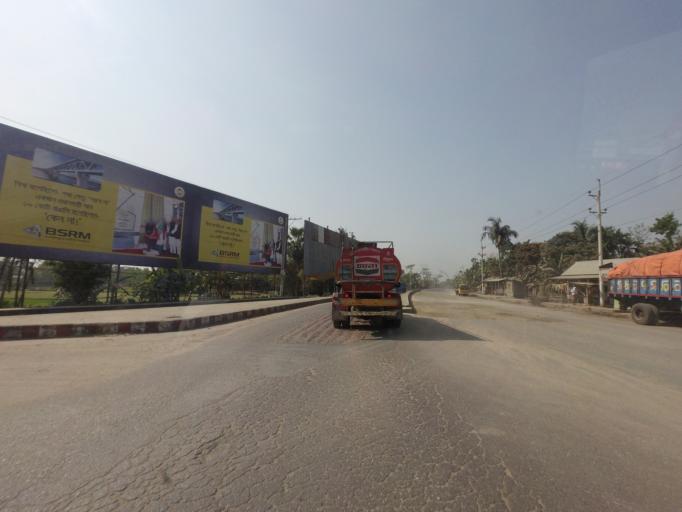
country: BD
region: Sylhet
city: Habiganj
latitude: 24.2948
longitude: 91.5103
